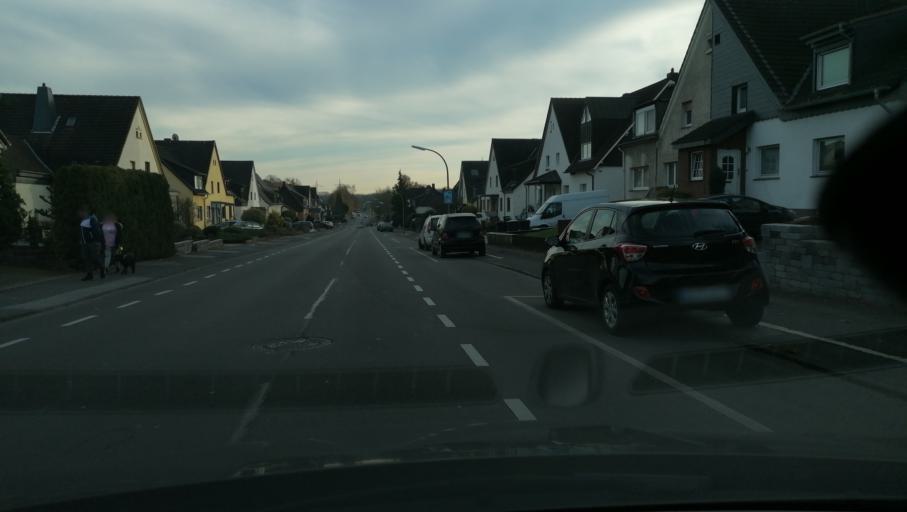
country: DE
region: North Rhine-Westphalia
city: Waltrop
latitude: 51.5562
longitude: 7.3825
